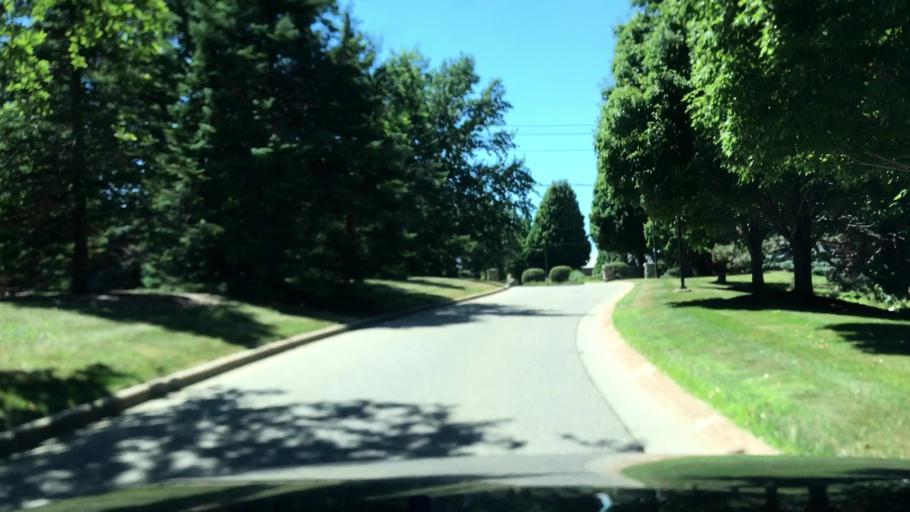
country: US
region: Michigan
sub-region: Ottawa County
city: Holland
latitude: 42.7721
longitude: -86.0763
